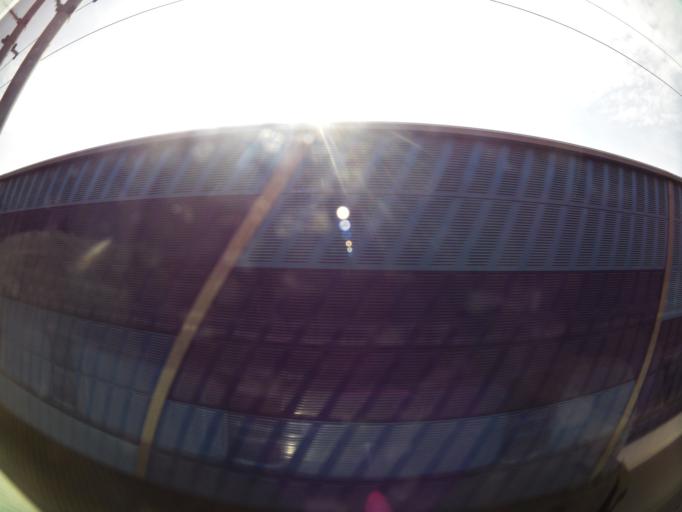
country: KR
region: Daejeon
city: Songgang-dong
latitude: 36.5351
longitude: 127.3525
